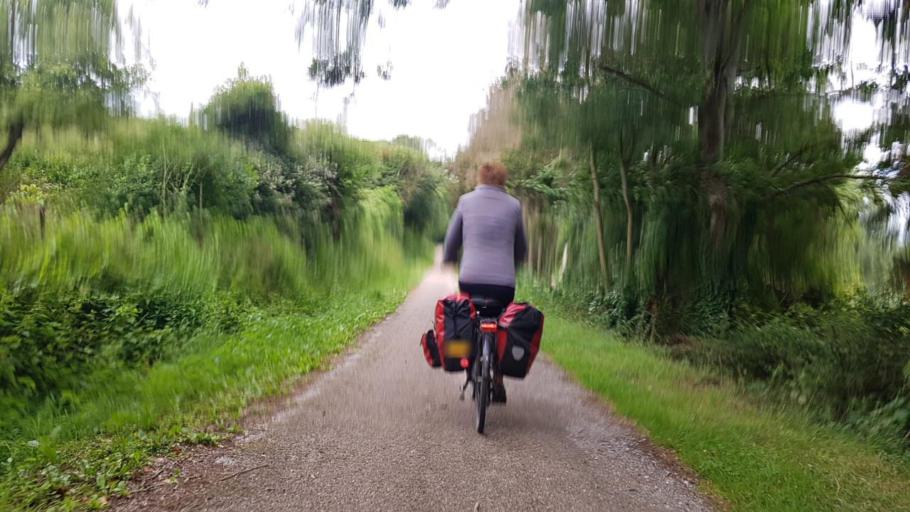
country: FR
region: Picardie
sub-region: Departement de l'Aisne
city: La Capelle
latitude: 49.9060
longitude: 3.9072
